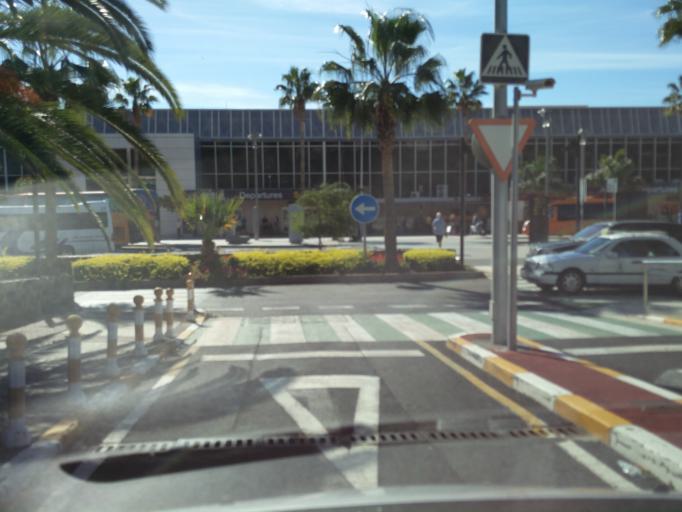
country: ES
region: Canary Islands
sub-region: Provincia de Santa Cruz de Tenerife
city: San Isidro
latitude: 28.0488
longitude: -16.5776
